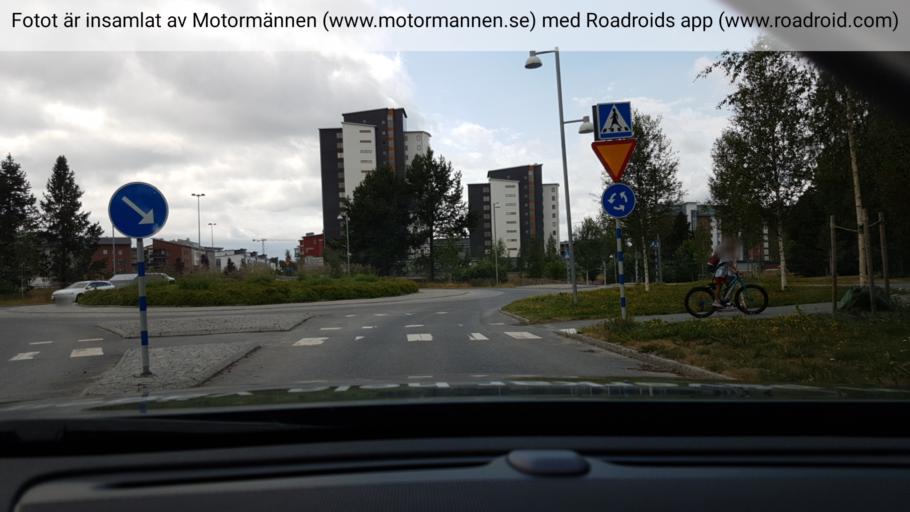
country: SE
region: Vaesterbotten
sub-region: Umea Kommun
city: Umea
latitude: 63.8364
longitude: 20.2316
